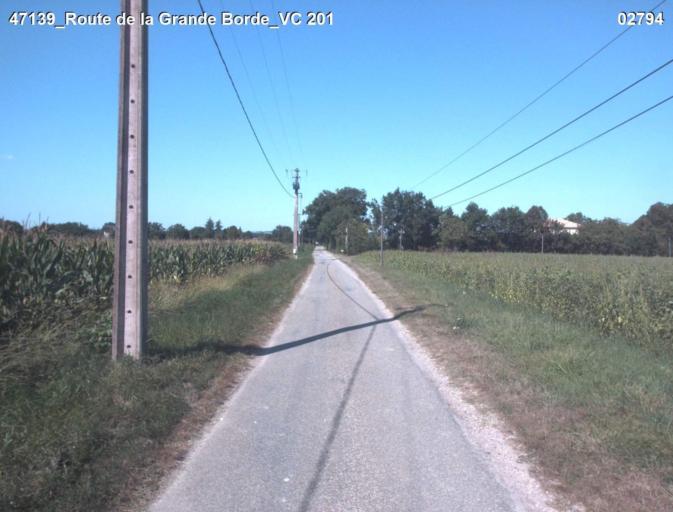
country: FR
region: Aquitaine
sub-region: Departement du Lot-et-Garonne
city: Nerac
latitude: 44.0840
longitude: 0.3815
